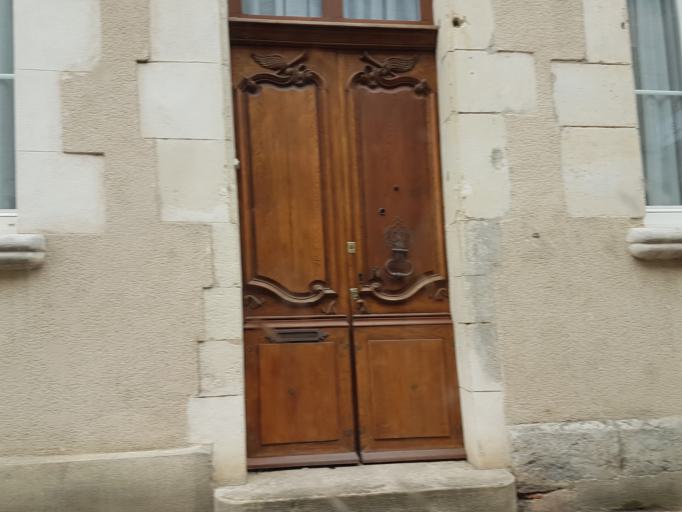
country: FR
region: Bourgogne
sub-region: Departement de la Nievre
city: Corbigny
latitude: 47.2567
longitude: 3.6834
